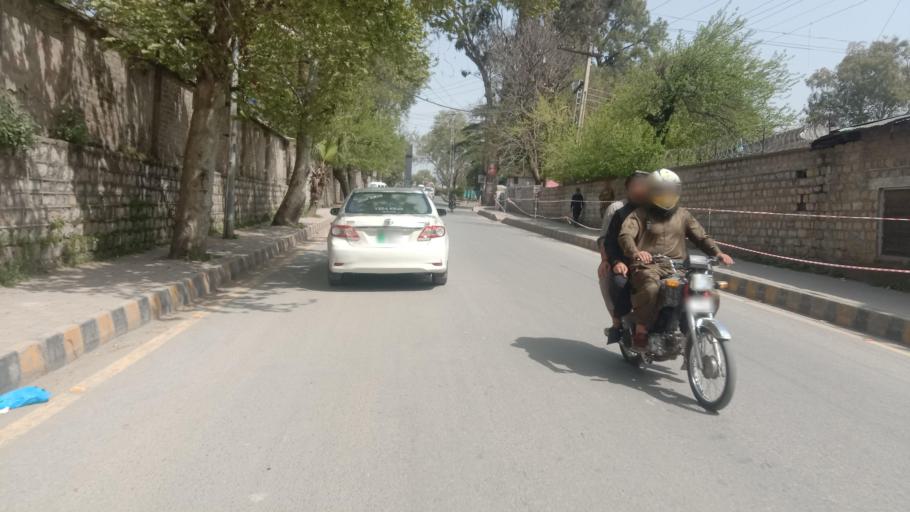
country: PK
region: Khyber Pakhtunkhwa
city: Abbottabad
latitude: 34.1484
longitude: 73.2134
